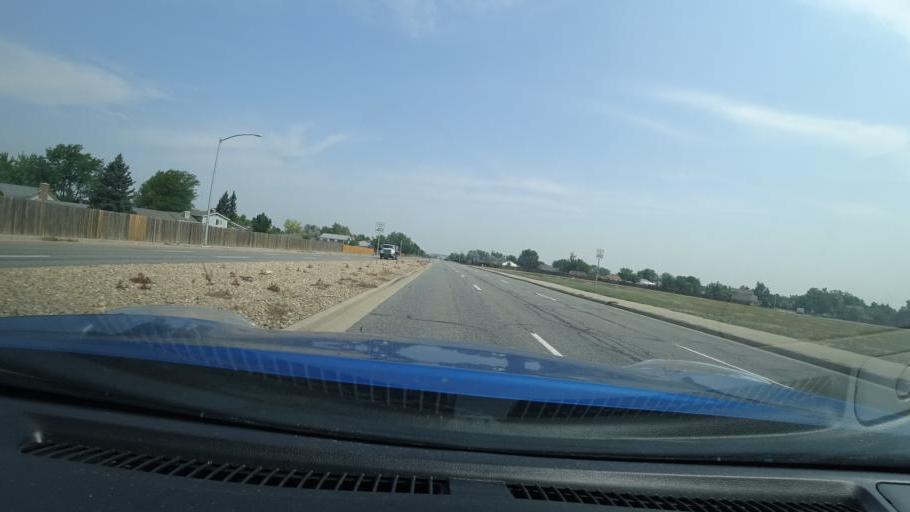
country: US
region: Colorado
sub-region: Adams County
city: Aurora
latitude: 39.6863
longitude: -104.7723
